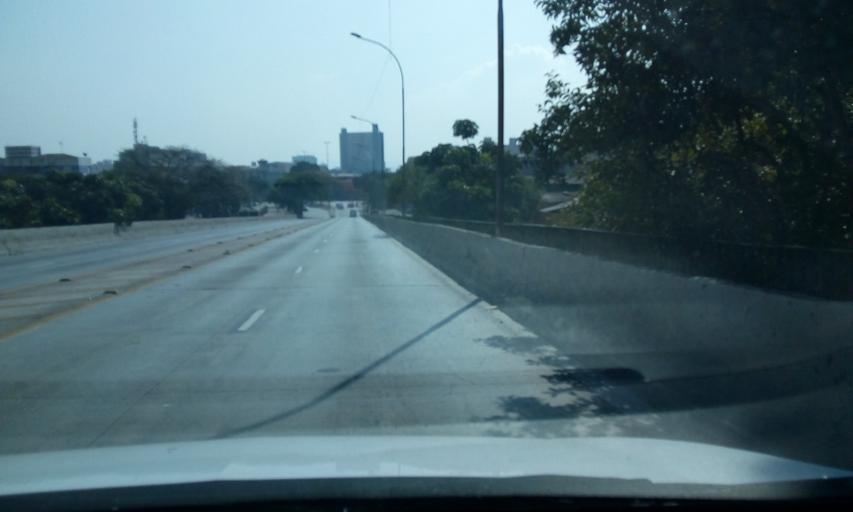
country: BR
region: Sao Paulo
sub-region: Sao Paulo
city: Sao Paulo
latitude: -23.5450
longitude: -46.6052
